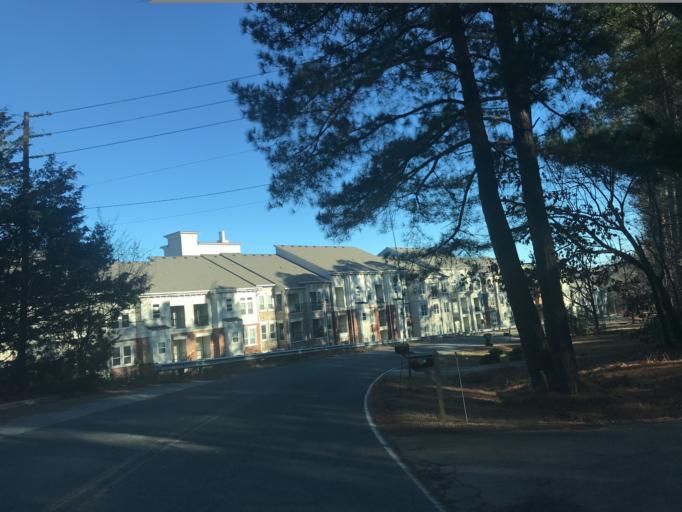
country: US
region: North Carolina
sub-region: Wake County
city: West Raleigh
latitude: 35.8394
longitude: -78.6847
